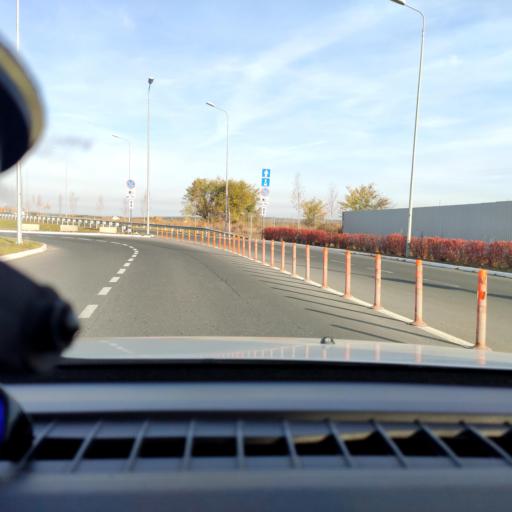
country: RU
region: Samara
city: Bereza
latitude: 53.5141
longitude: 50.1582
